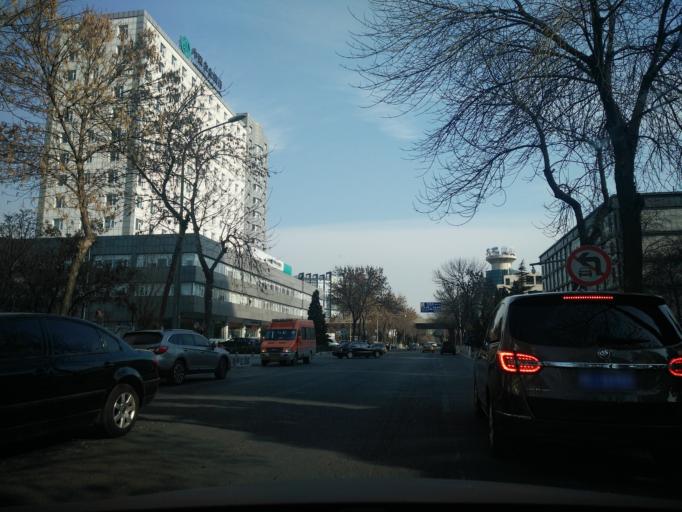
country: CN
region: Beijing
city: Jiugong
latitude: 39.7953
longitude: 116.5024
